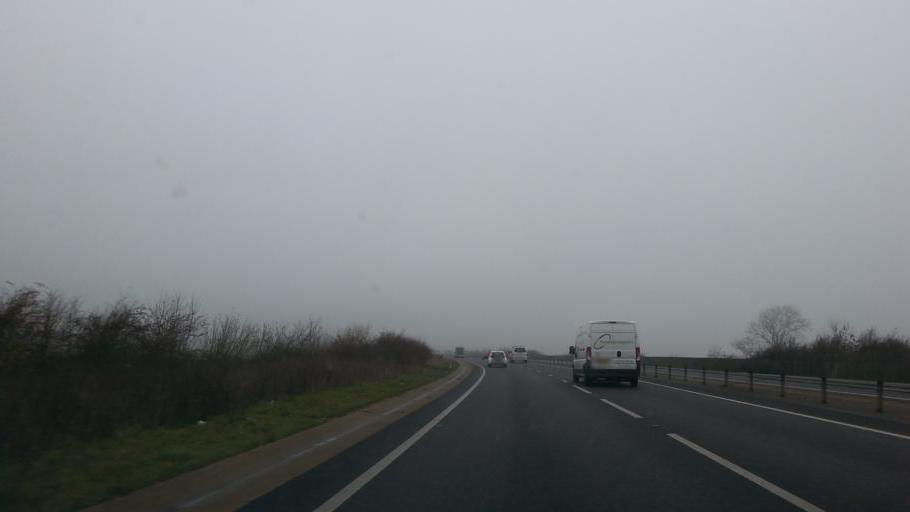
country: GB
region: England
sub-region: Cambridgeshire
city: Papworth Everard
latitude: 52.2279
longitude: -0.0833
